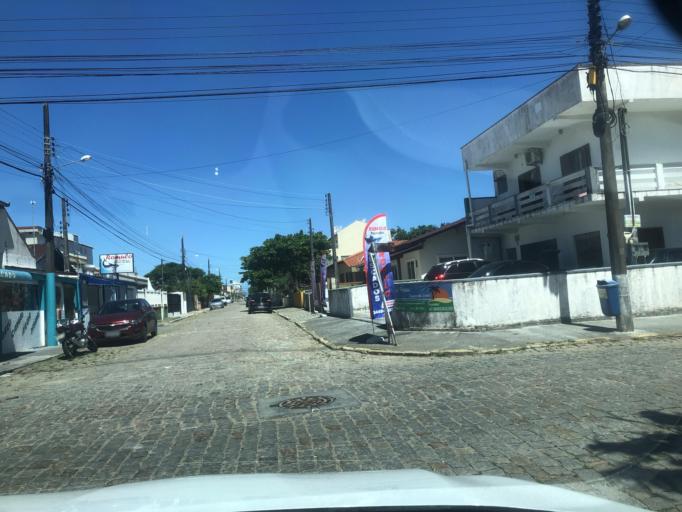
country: BR
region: Santa Catarina
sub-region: Sao Francisco Do Sul
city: Sao Francisco do Sul
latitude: -26.2281
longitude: -48.5102
